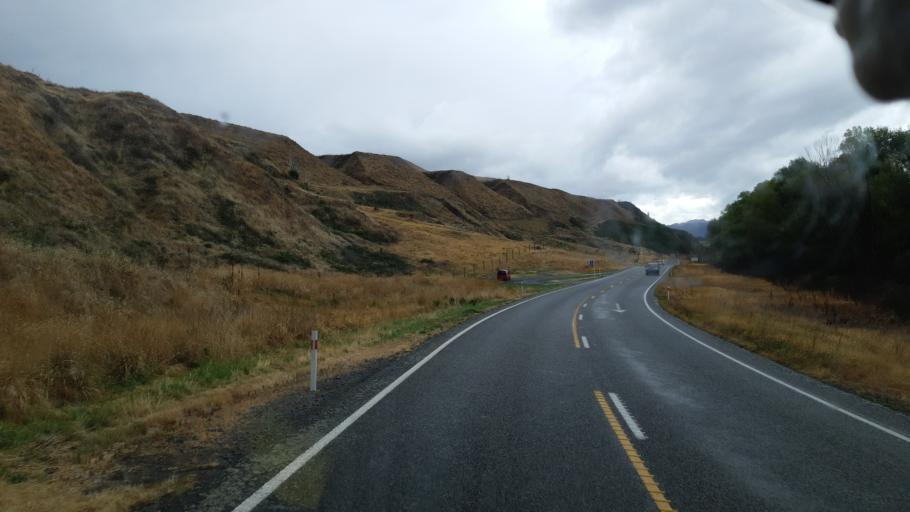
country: NZ
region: Canterbury
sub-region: Hurunui District
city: Amberley
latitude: -42.5785
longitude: 172.7500
